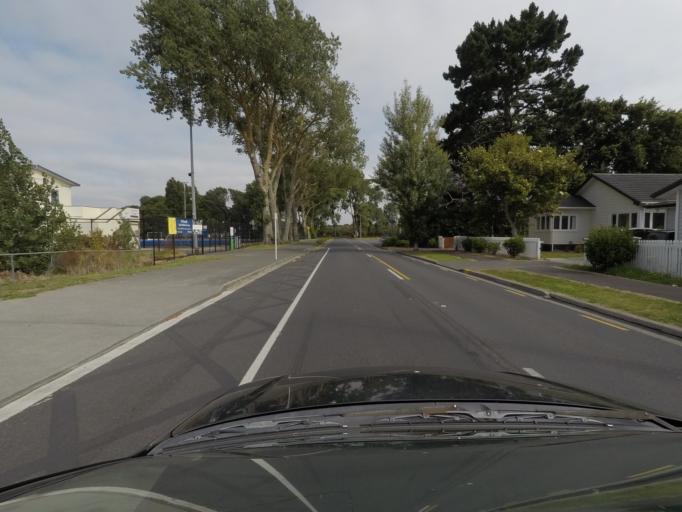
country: NZ
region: Auckland
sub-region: Auckland
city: Auckland
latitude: -36.9119
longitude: 174.7434
